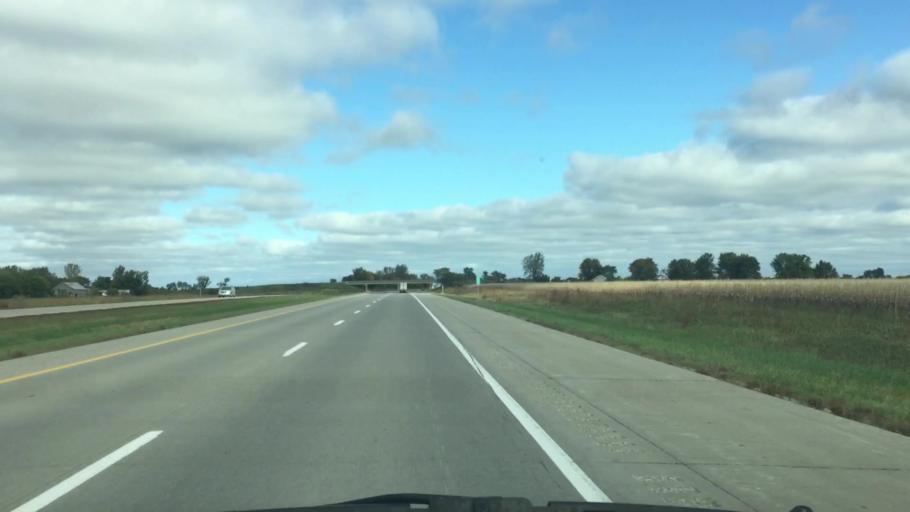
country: US
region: Iowa
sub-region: Clarke County
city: Osceola
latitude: 40.9374
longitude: -93.7987
